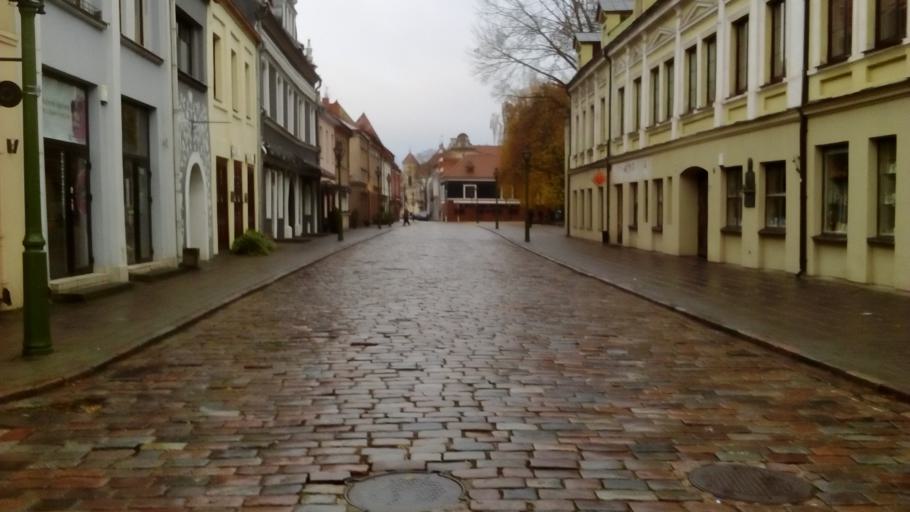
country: LT
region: Kauno apskritis
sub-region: Kaunas
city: Kaunas
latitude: 54.8966
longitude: 23.8901
